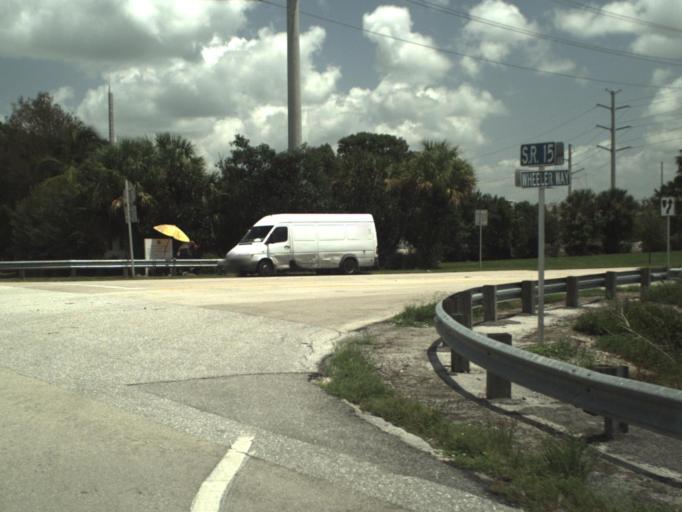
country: US
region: Florida
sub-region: Palm Beach County
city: Belle Glade
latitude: 26.7212
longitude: -80.6679
